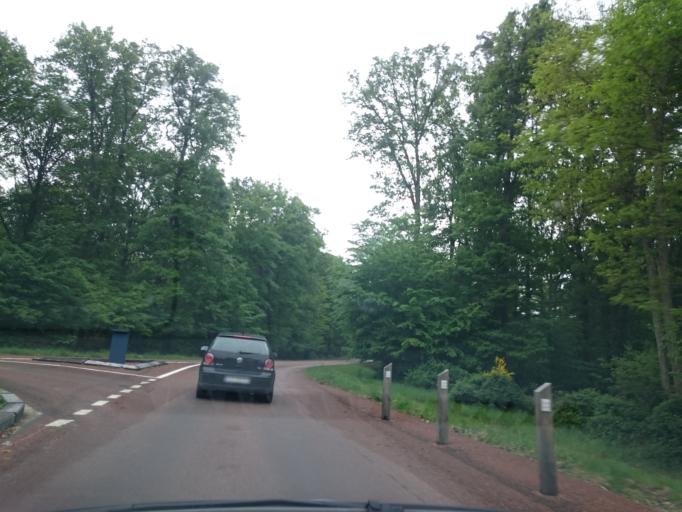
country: FR
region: Centre
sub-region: Departement du Loir-et-Cher
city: Muides-sur-Loire
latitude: 47.6372
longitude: 1.5196
